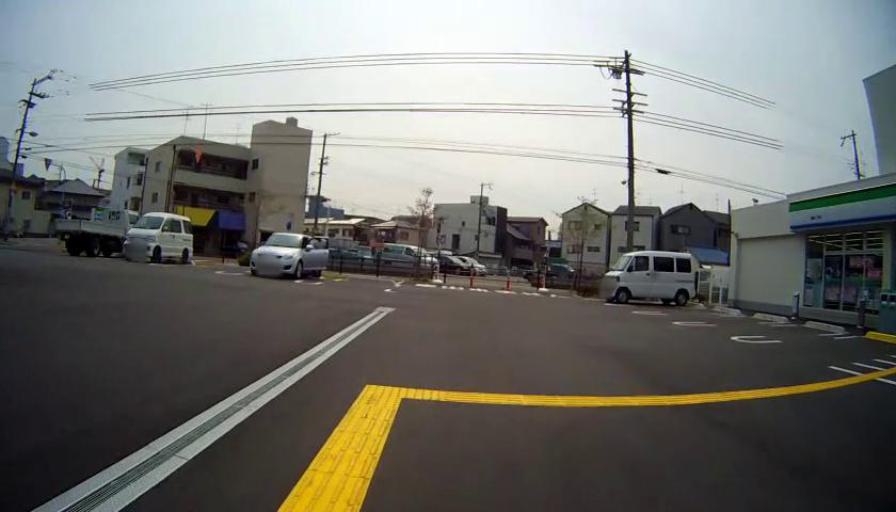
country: JP
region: Osaka
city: Moriguchi
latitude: 34.7457
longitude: 135.5414
